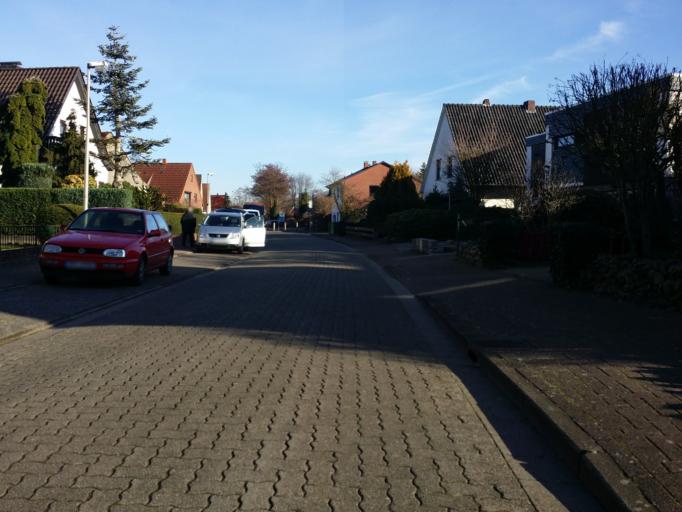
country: DE
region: Lower Saxony
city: Delmenhorst
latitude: 53.0544
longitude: 8.6697
